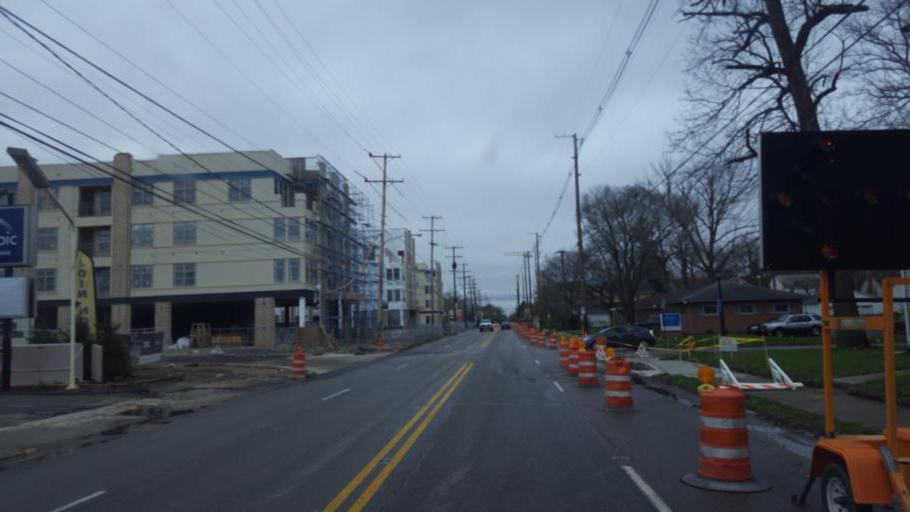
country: US
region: Ohio
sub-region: Franklin County
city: Worthington
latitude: 40.0353
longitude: -83.0008
